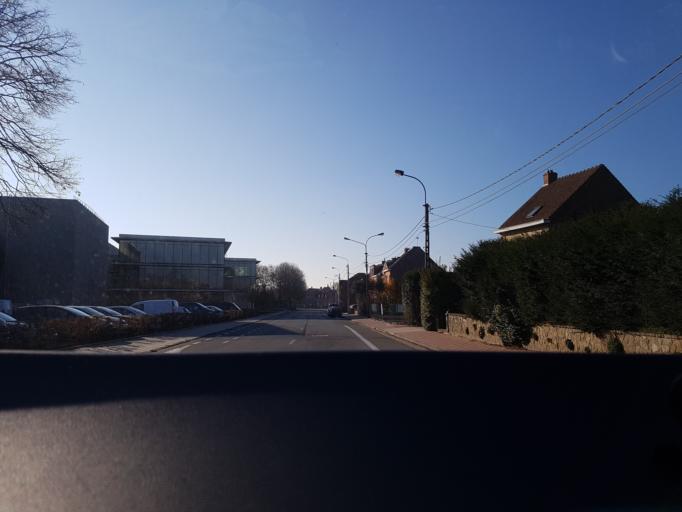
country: FR
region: Nord-Pas-de-Calais
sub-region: Departement du Nord
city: Deulemont
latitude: 50.7437
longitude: 2.9344
